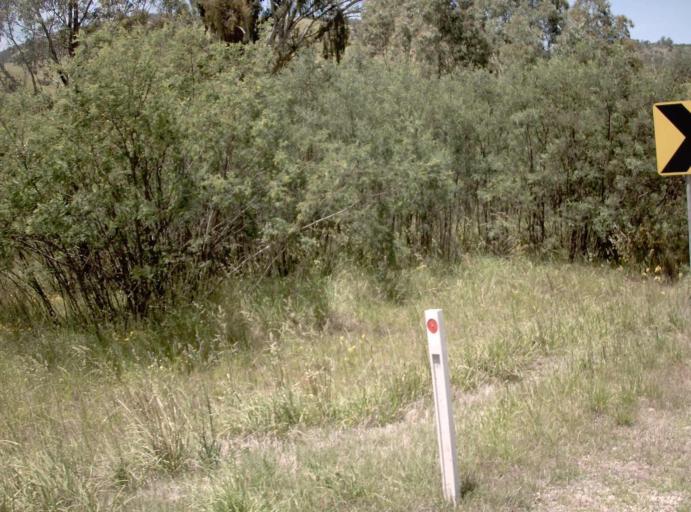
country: AU
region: Victoria
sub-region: East Gippsland
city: Bairnsdale
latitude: -37.5125
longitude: 147.8475
